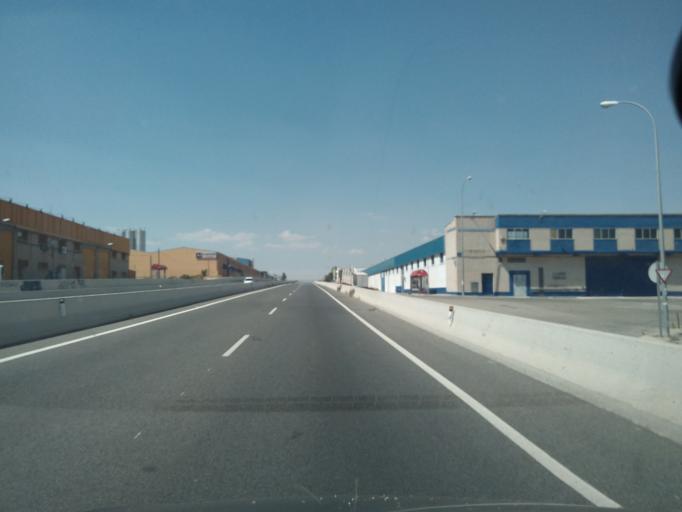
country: ES
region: Madrid
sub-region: Provincia de Madrid
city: Ajalvir
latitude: 40.5088
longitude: -3.4801
